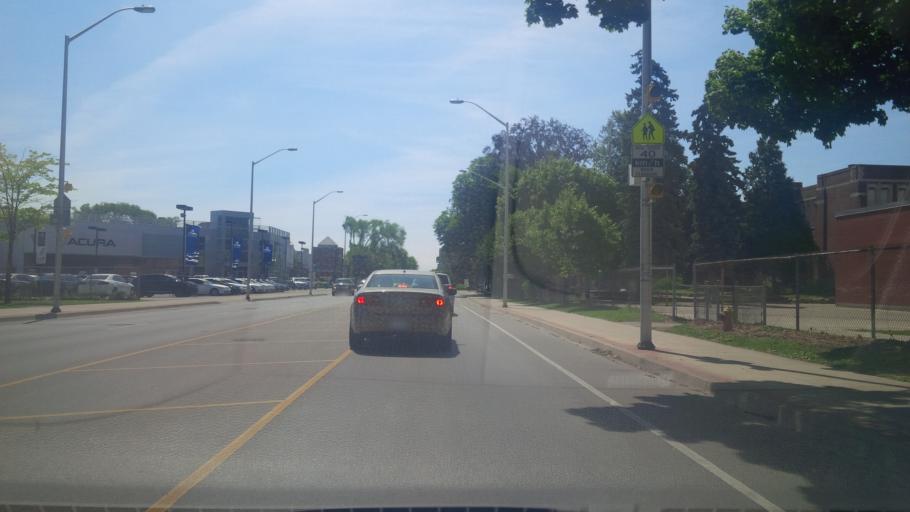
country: CA
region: Ontario
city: Burlington
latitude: 43.3307
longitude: -79.8052
